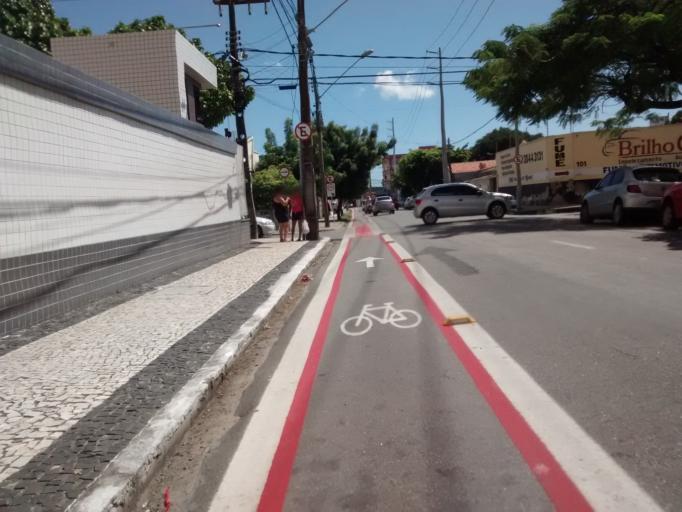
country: BR
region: Ceara
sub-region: Fortaleza
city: Fortaleza
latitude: -3.7357
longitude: -38.5573
